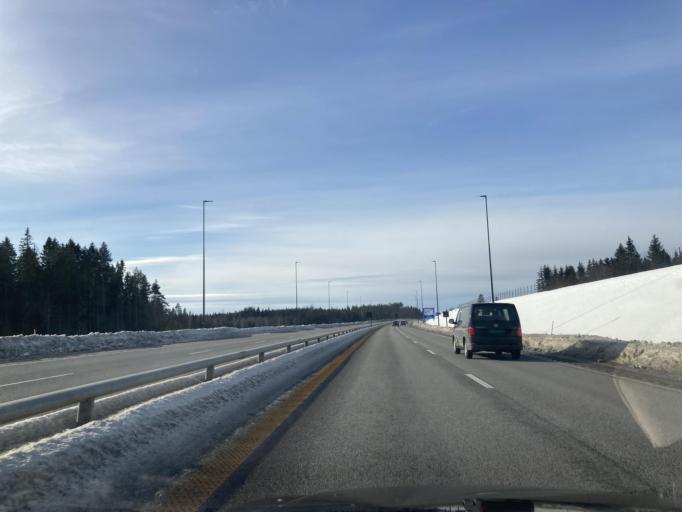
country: NO
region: Hedmark
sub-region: Loten
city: Loten
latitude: 60.8551
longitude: 11.3959
